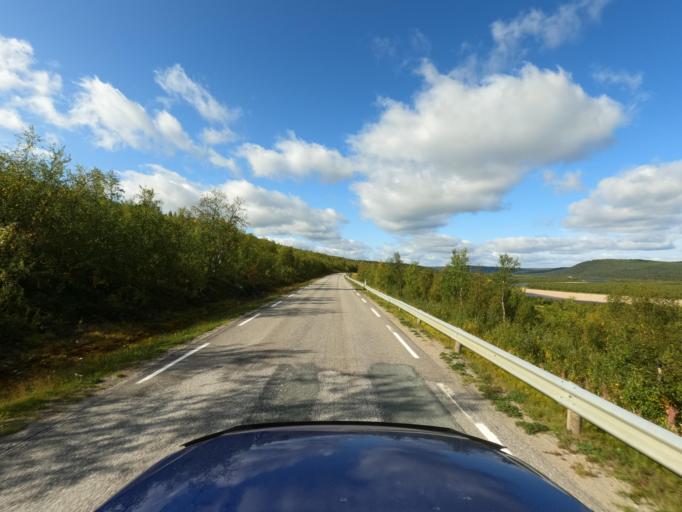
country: NO
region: Finnmark Fylke
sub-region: Karasjok
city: Karasjohka
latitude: 69.4378
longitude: 25.6589
